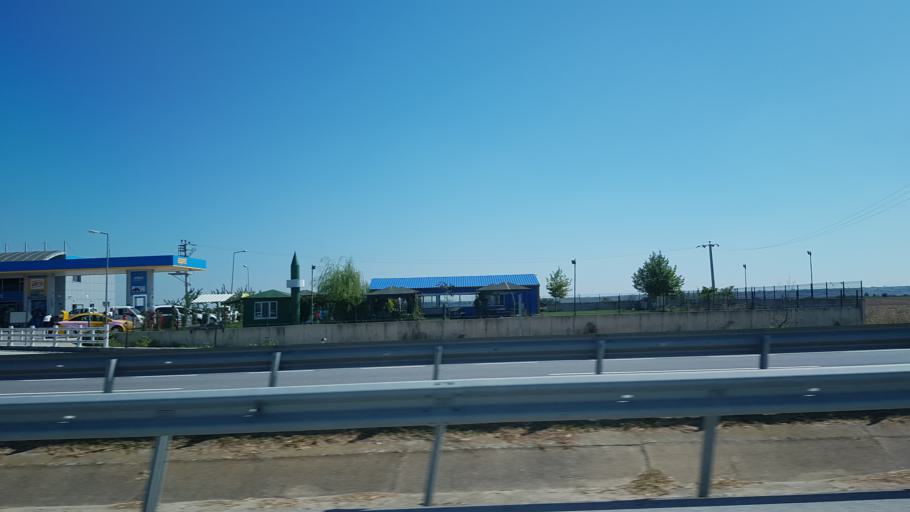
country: TR
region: Kirklareli
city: Inece
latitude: 41.5705
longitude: 27.1467
